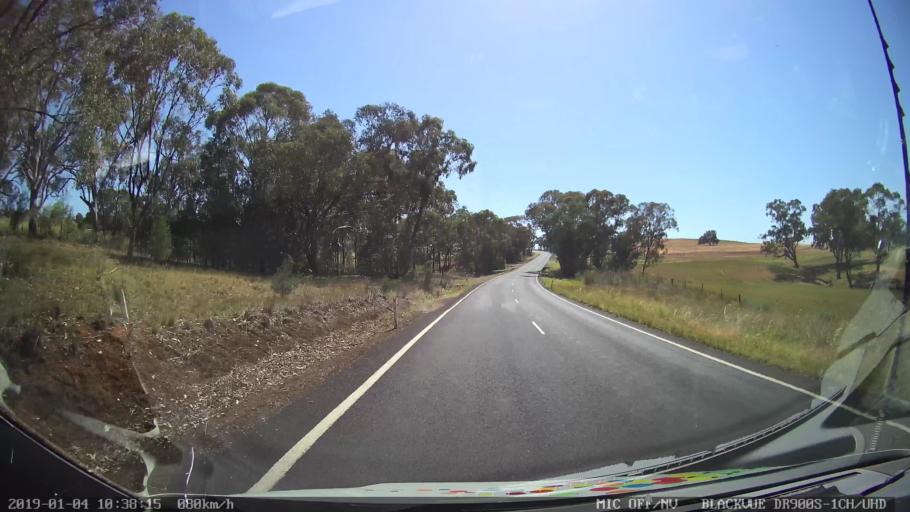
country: AU
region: New South Wales
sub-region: Cabonne
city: Molong
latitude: -33.2934
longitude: 148.7062
